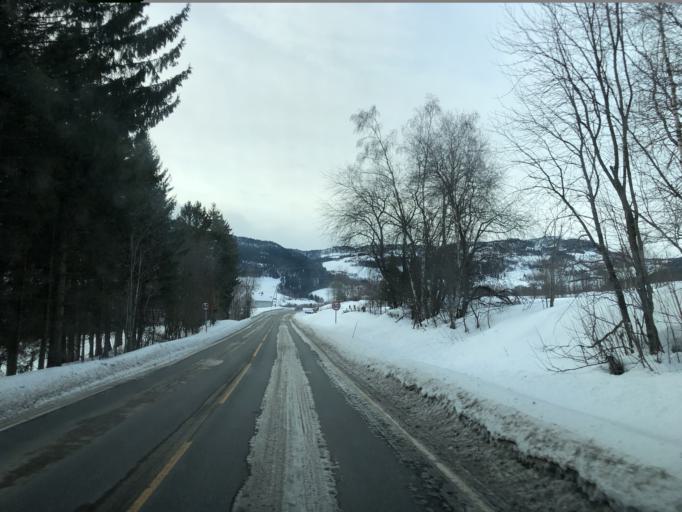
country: NO
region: Oppland
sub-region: Gausdal
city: Segalstad bru
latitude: 61.2607
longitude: 10.1627
